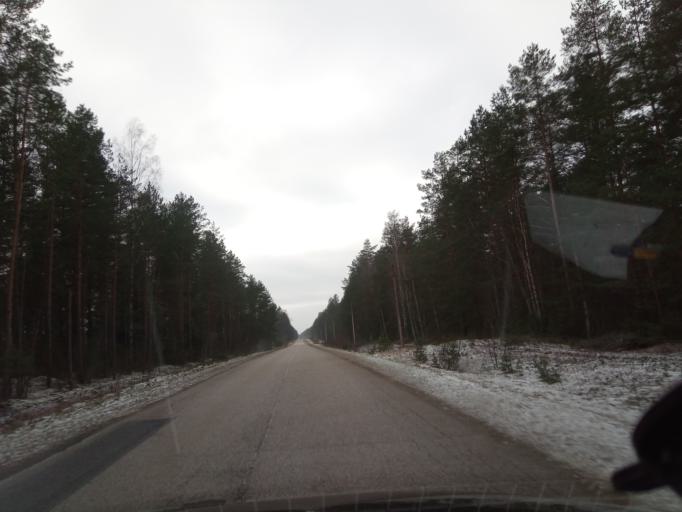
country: LT
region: Alytaus apskritis
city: Varena
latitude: 54.0418
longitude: 24.3784
